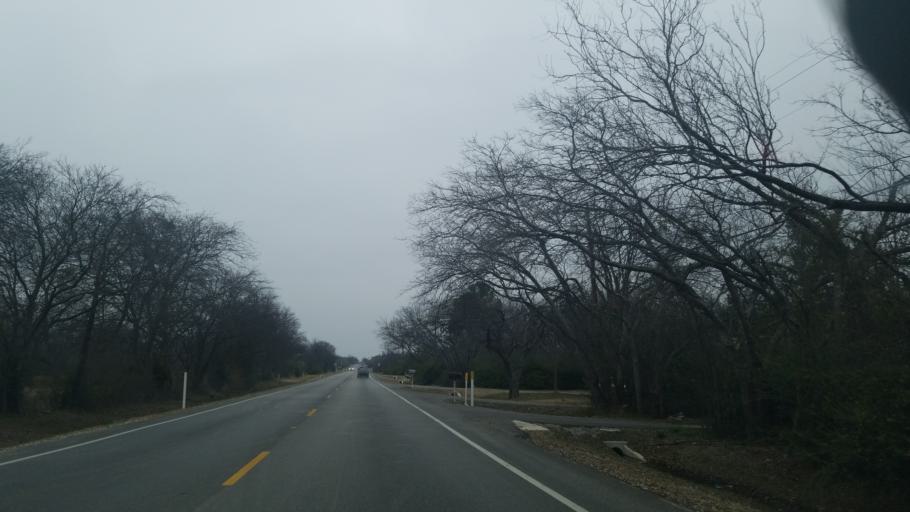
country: US
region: Texas
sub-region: Denton County
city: Denton
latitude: 33.1638
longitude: -97.1419
